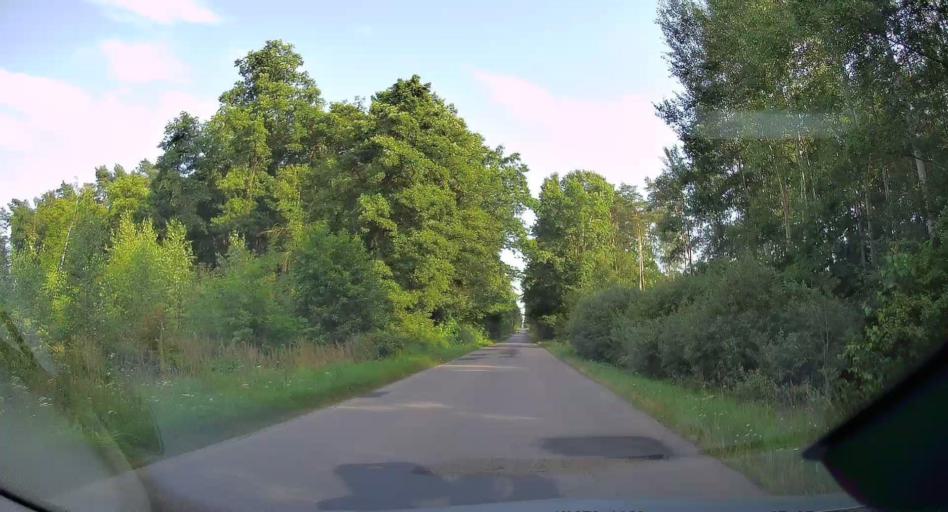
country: PL
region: Swietokrzyskie
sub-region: Powiat konecki
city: Konskie
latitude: 51.2273
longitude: 20.3839
